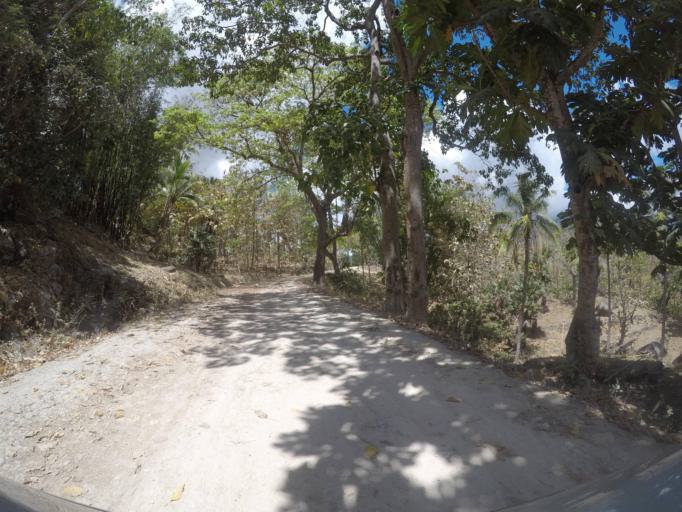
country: TL
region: Baucau
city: Baucau
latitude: -8.4887
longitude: 126.6469
